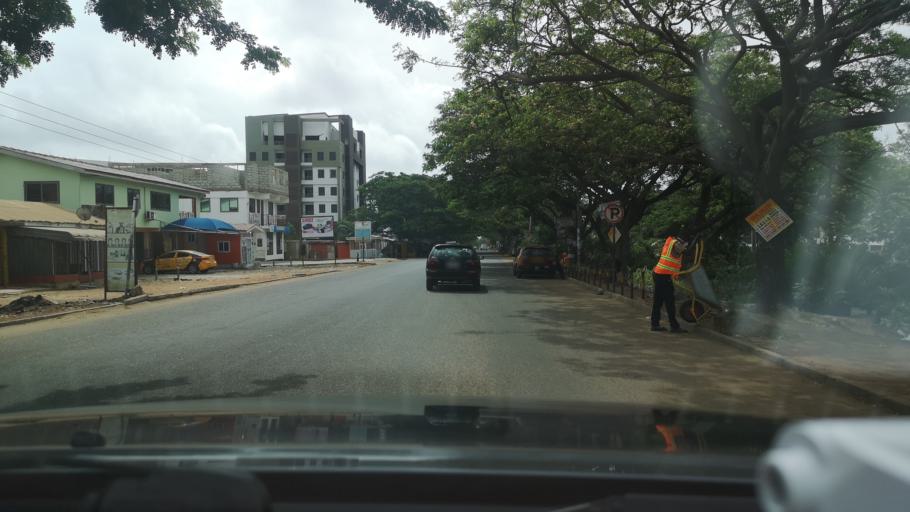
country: GH
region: Greater Accra
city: Nungua
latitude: 5.6240
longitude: -0.0689
